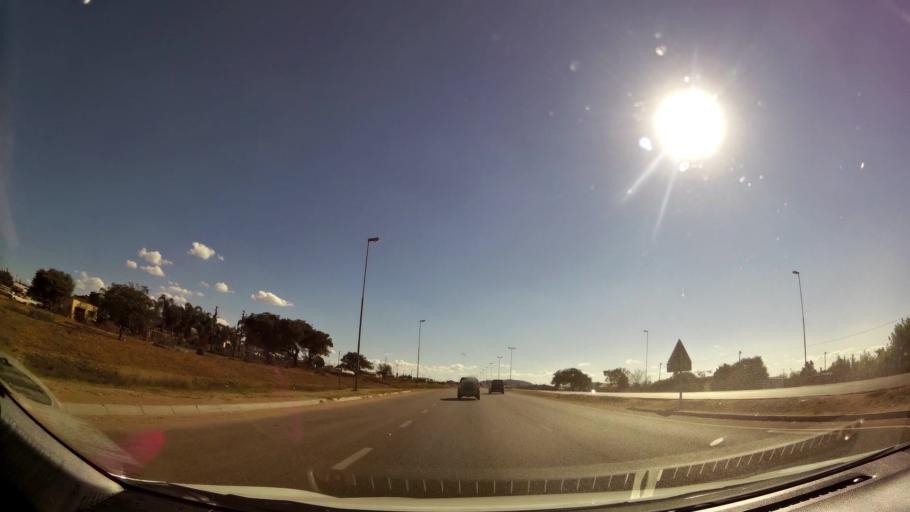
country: ZA
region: Limpopo
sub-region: Capricorn District Municipality
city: Mankoeng
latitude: -23.8925
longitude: 29.7131
